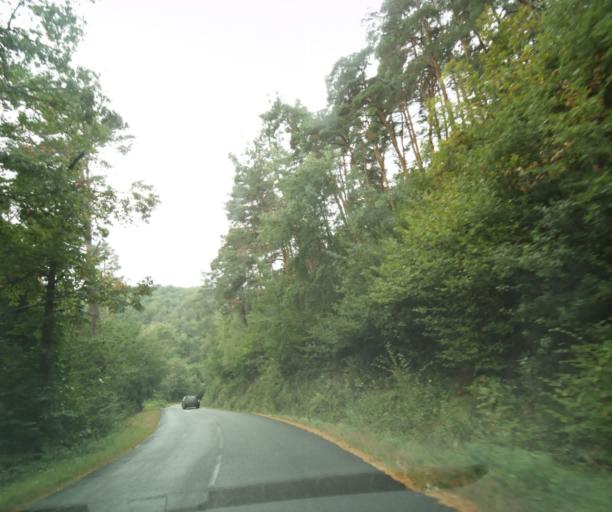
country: FR
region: Auvergne
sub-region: Departement du Puy-de-Dome
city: Durtol
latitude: 45.7930
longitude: 3.0399
